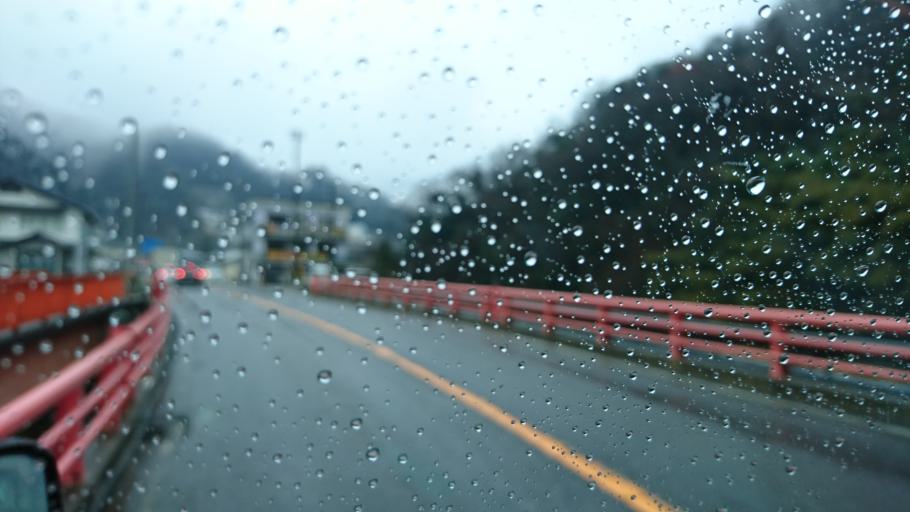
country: JP
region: Tottori
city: Tottori
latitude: 35.5604
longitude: 134.4855
